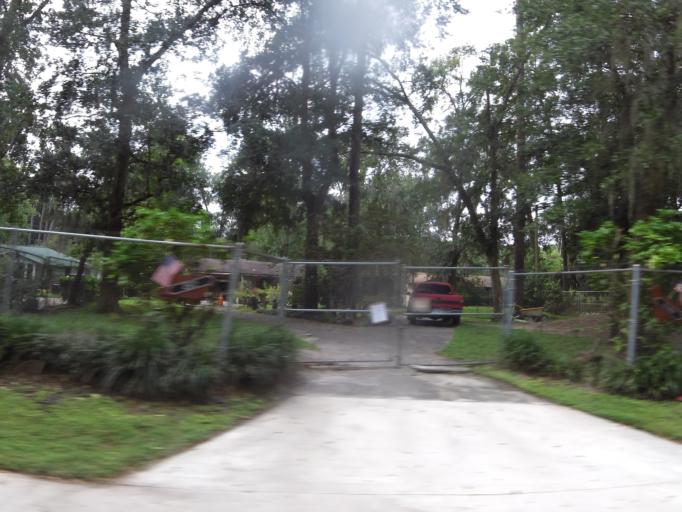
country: US
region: Florida
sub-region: Clay County
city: Bellair-Meadowbrook Terrace
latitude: 30.2597
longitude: -81.7223
